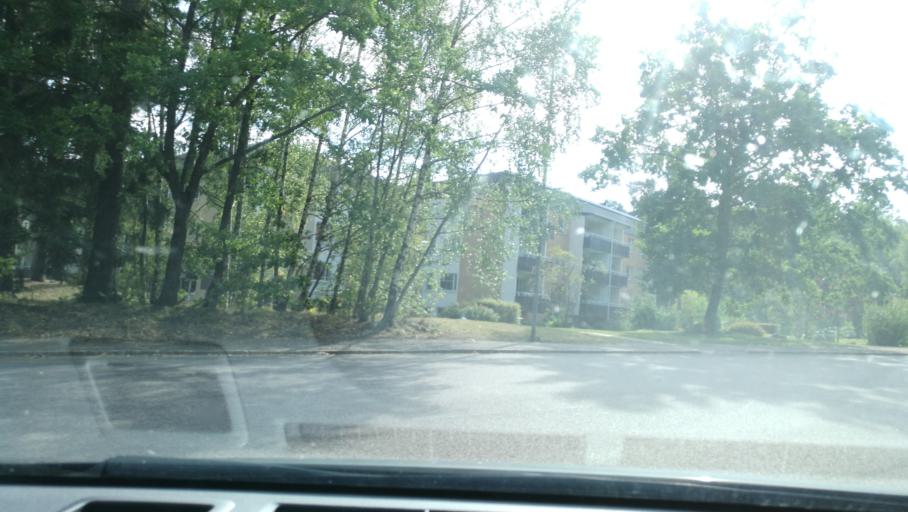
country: SE
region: Vaestmanland
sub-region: Vasteras
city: Vasteras
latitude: 59.6087
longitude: 16.5069
